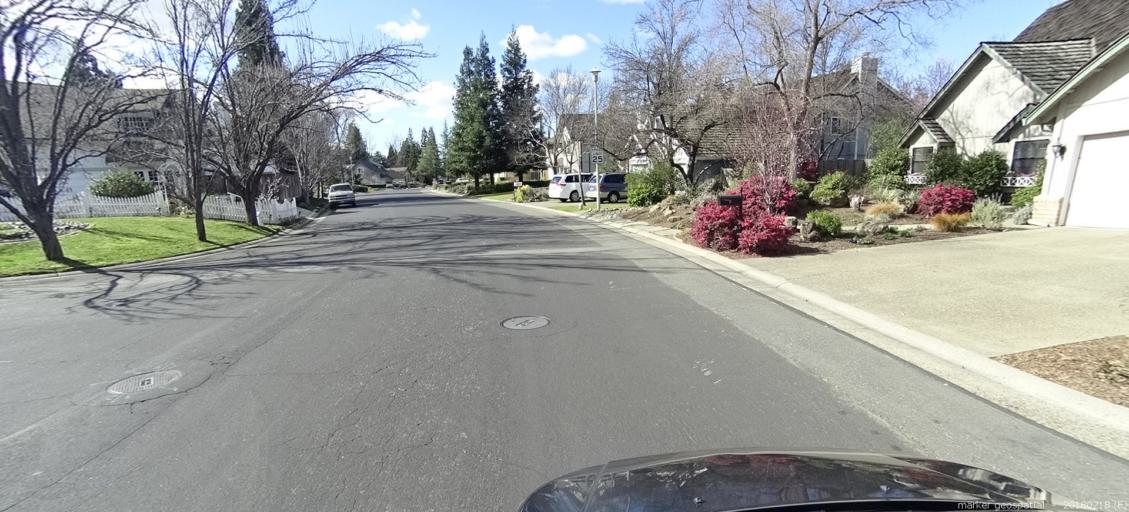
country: US
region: California
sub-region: Sacramento County
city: Folsom
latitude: 38.6886
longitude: -121.1878
